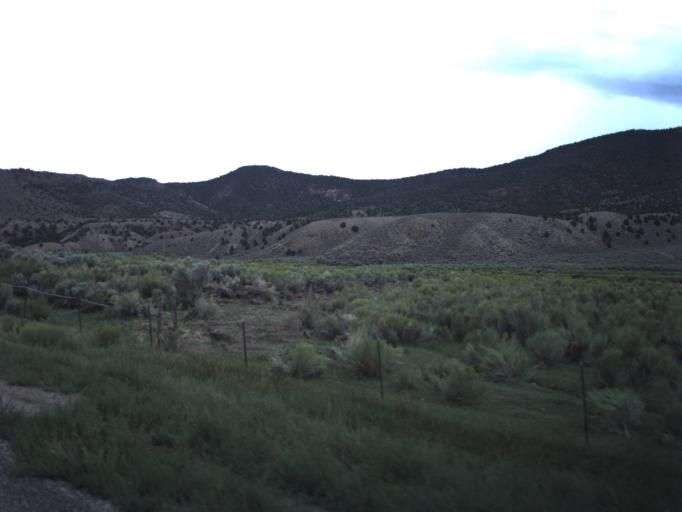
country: US
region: Utah
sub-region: Piute County
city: Junction
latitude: 38.1689
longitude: -112.0559
